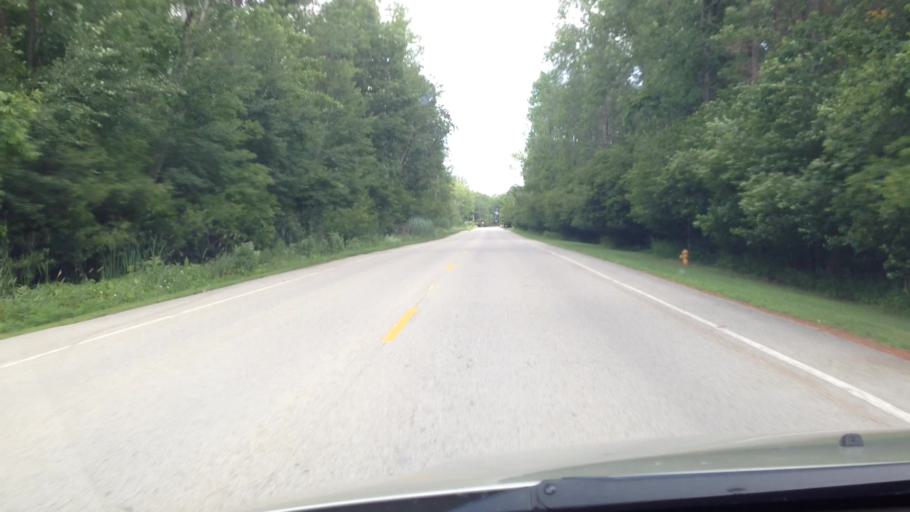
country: US
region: Michigan
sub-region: Menominee County
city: Menominee
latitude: 45.1441
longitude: -87.6104
